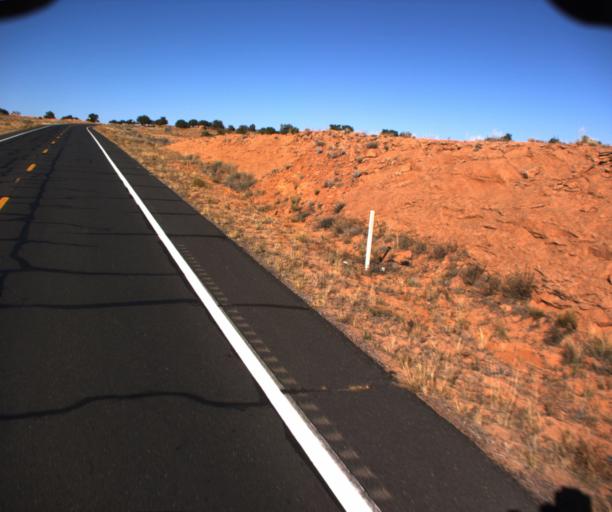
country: US
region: Arizona
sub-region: Coconino County
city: Kaibito
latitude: 36.5028
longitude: -110.7058
